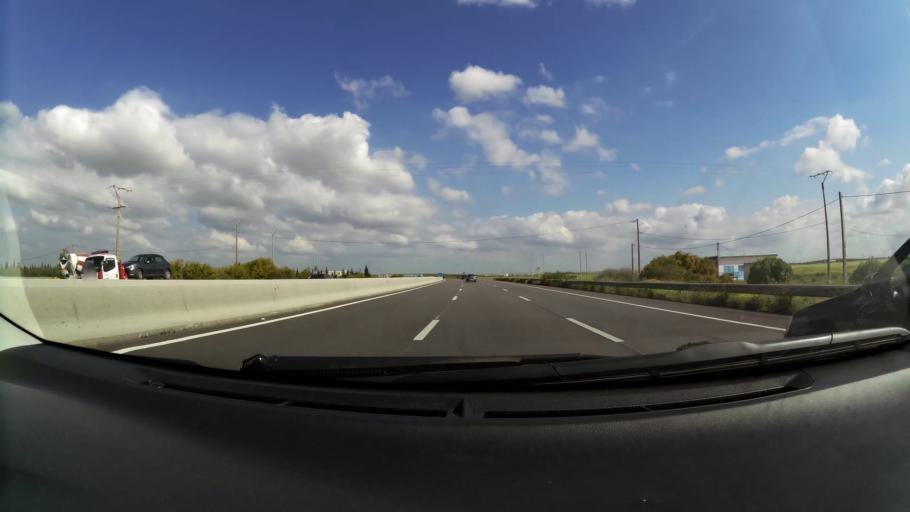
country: MA
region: Chaouia-Ouardigha
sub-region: Settat Province
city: Berrechid
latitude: 33.3161
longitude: -7.6009
